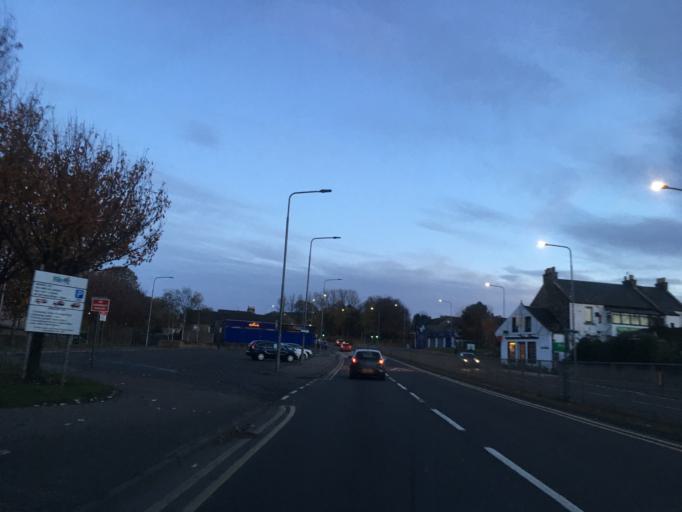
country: GB
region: Scotland
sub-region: Fife
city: Dunfermline
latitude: 56.0636
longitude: -3.4497
